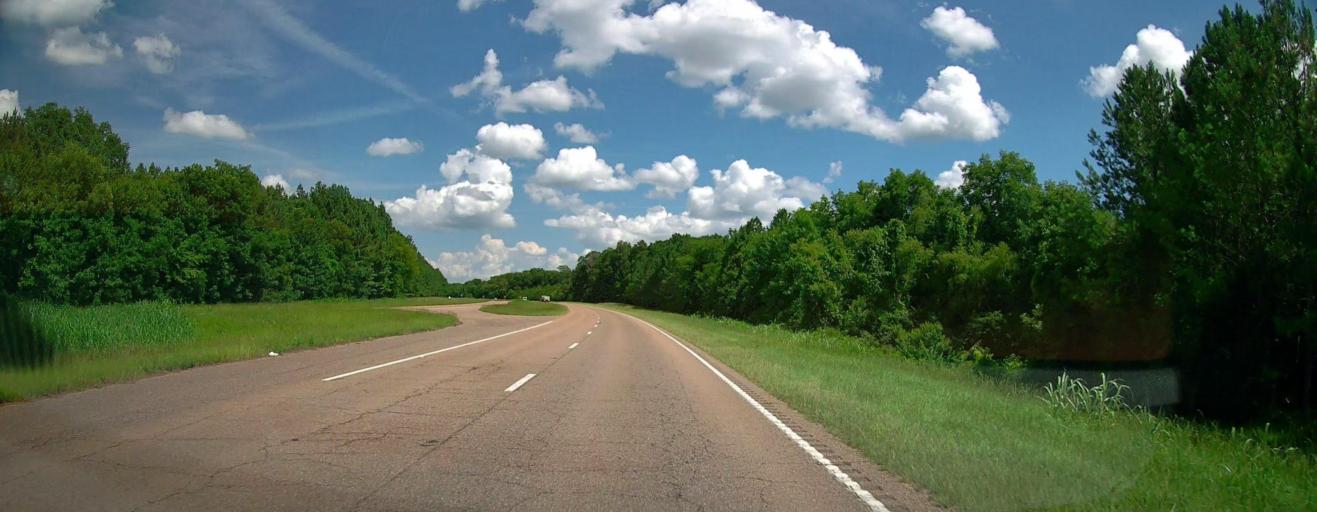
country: US
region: Mississippi
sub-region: Monroe County
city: Aberdeen
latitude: 33.8175
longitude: -88.5790
